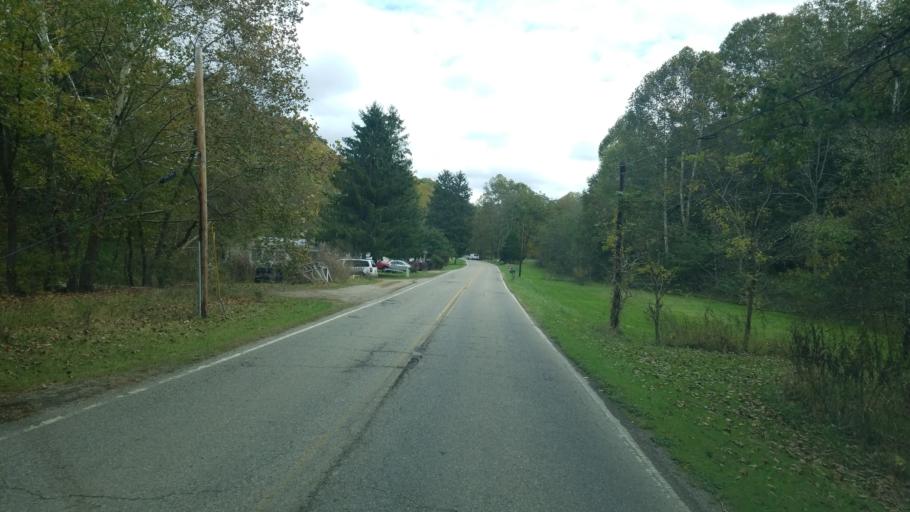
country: US
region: Ohio
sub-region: Jackson County
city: Jackson
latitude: 39.0736
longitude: -82.6006
